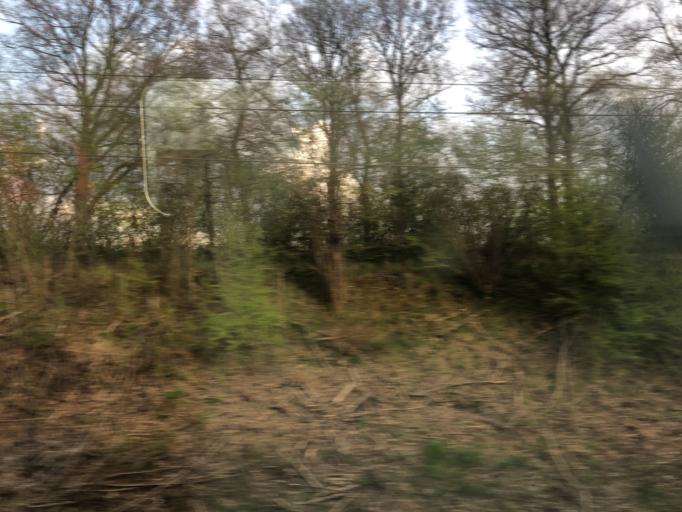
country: DK
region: Zealand
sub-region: Roskilde Kommune
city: Roskilde
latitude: 55.6259
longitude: 12.0646
